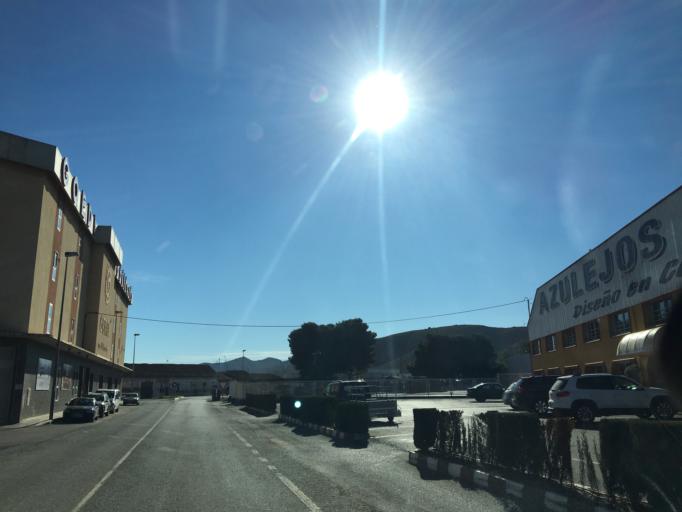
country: ES
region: Murcia
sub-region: Murcia
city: La Union
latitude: 37.6445
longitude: -0.8717
